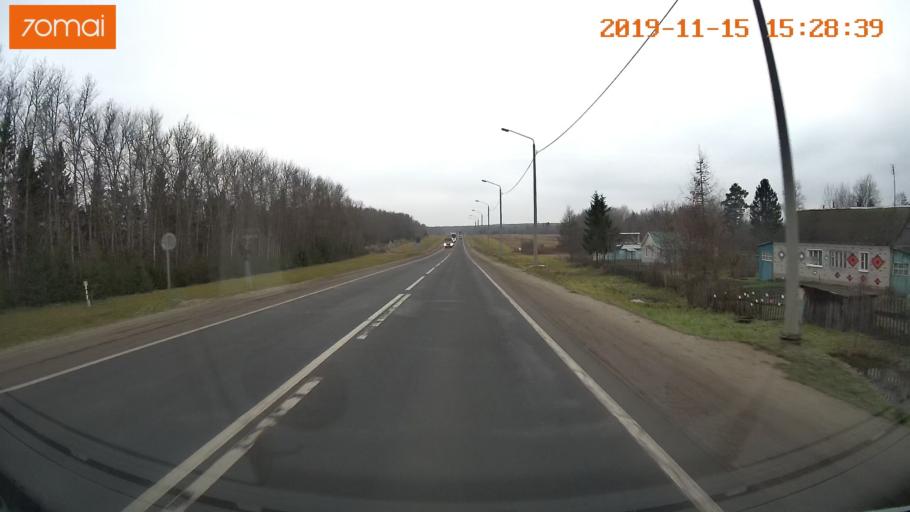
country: RU
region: Jaroslavl
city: Danilov
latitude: 58.1298
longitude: 40.1320
